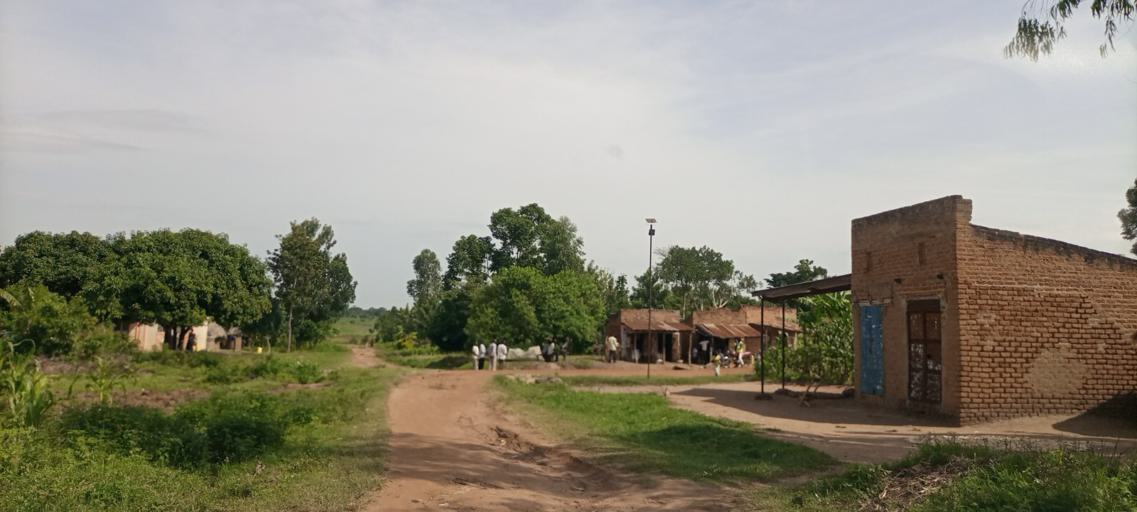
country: UG
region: Eastern Region
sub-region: Budaka District
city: Budaka
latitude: 1.1369
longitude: 34.0145
